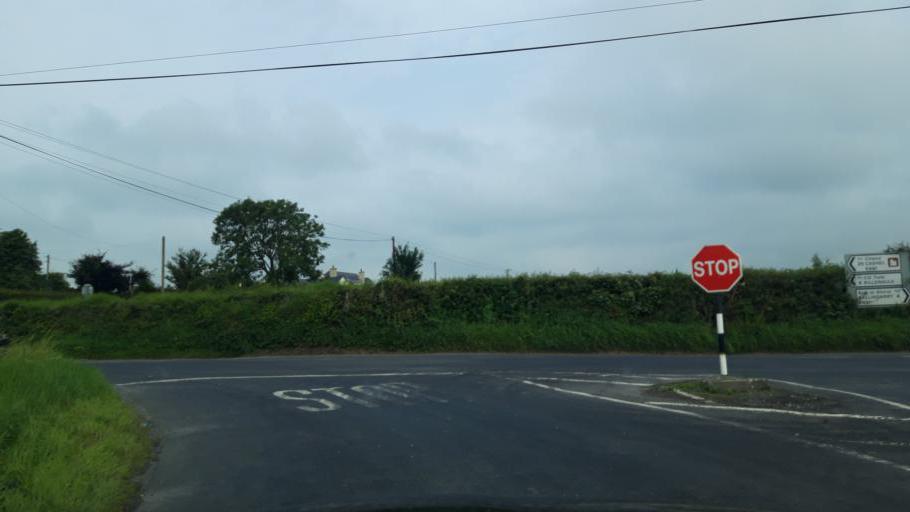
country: IE
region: Munster
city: Fethard
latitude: 52.5871
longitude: -7.5923
